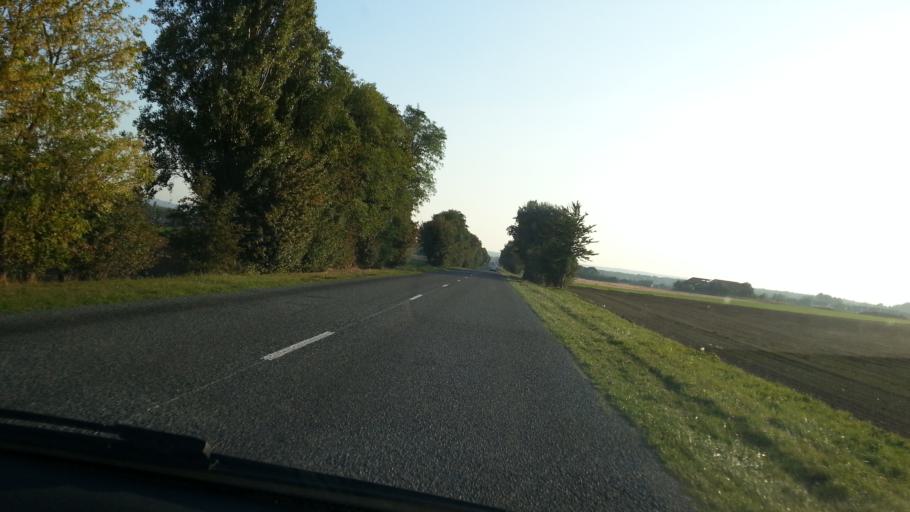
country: FR
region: Picardie
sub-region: Departement de l'Oise
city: Saint-Martin-Longueau
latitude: 49.3516
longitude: 2.6094
